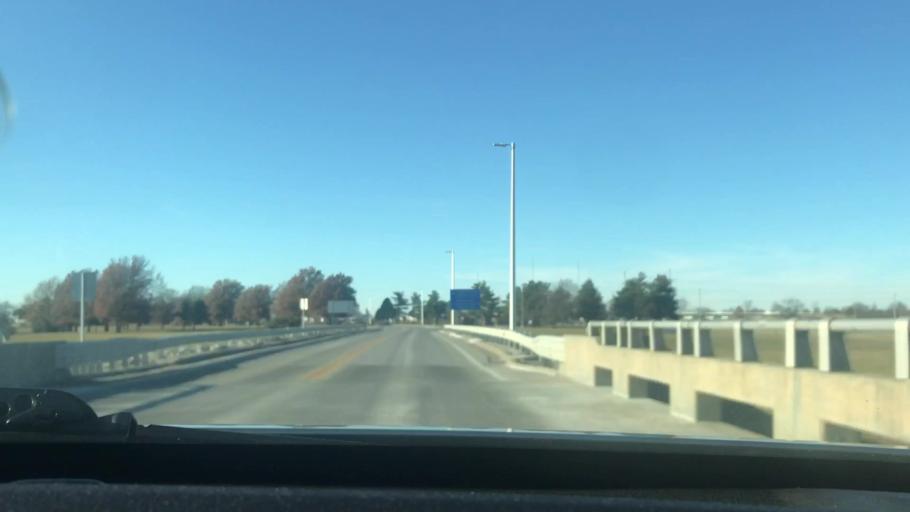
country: US
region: Missouri
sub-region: Platte County
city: Weatherby Lake
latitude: 39.3104
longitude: -94.7095
